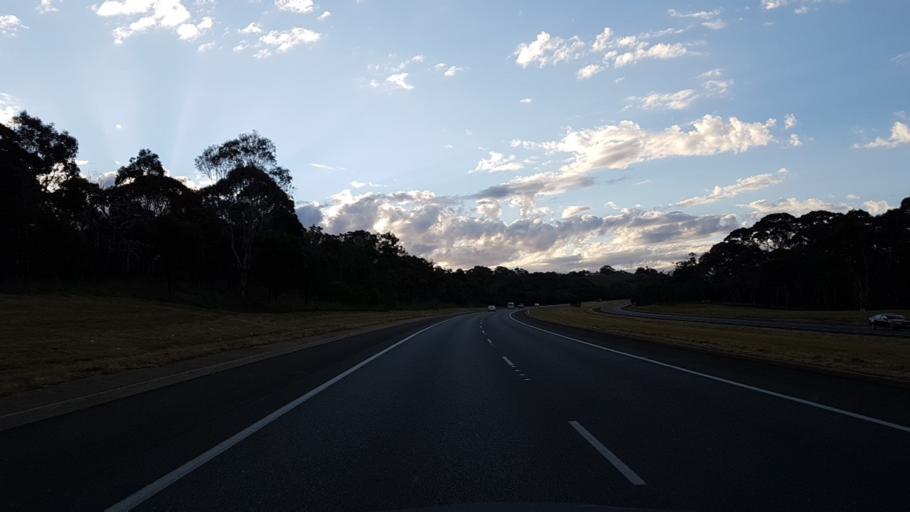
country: AU
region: South Australia
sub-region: Mount Barker
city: Little Hampton
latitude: -35.0589
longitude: 138.8408
